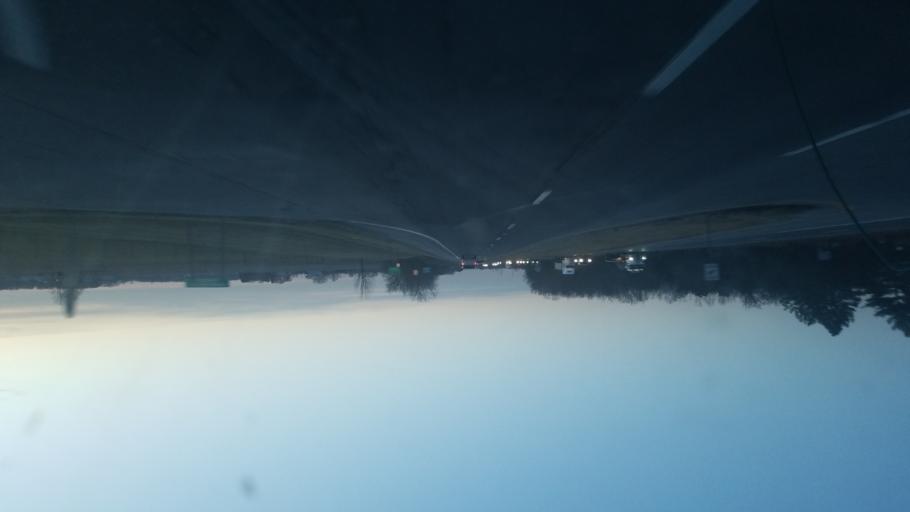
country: US
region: Ohio
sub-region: Marion County
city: Marion
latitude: 40.4937
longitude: -83.0748
